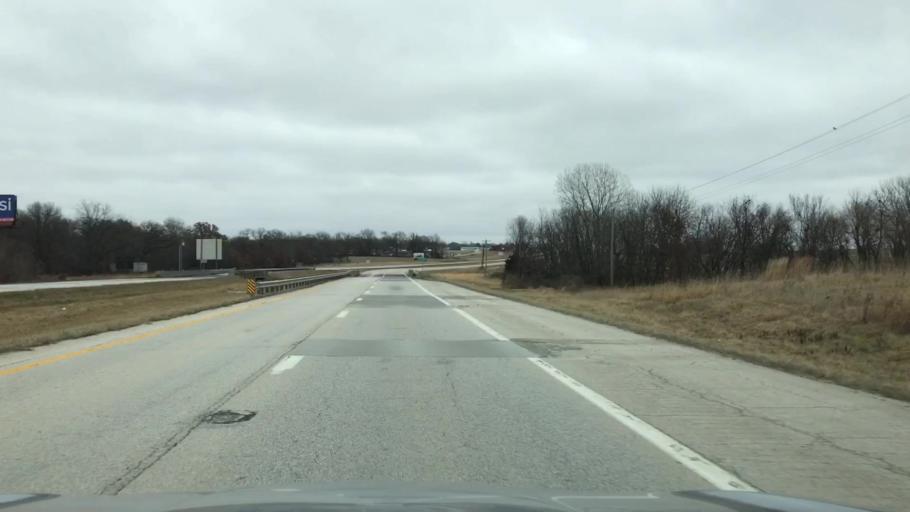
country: US
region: Missouri
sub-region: Livingston County
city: Chillicothe
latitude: 39.7745
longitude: -93.5325
